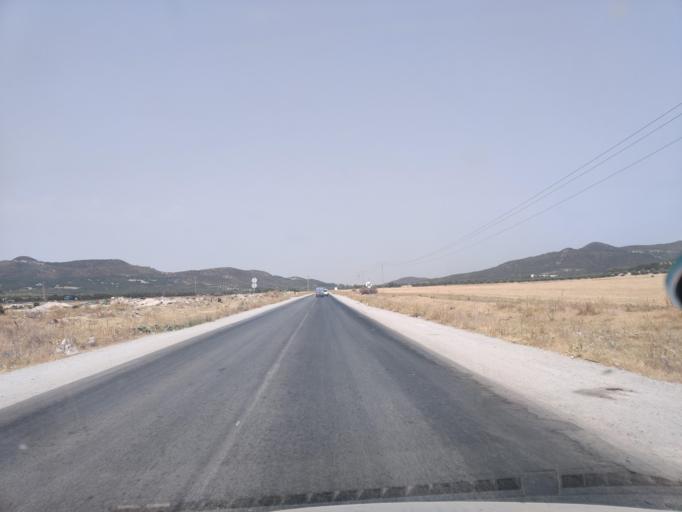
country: TN
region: Tunis
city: Hammam-Lif
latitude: 36.6205
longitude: 10.4097
